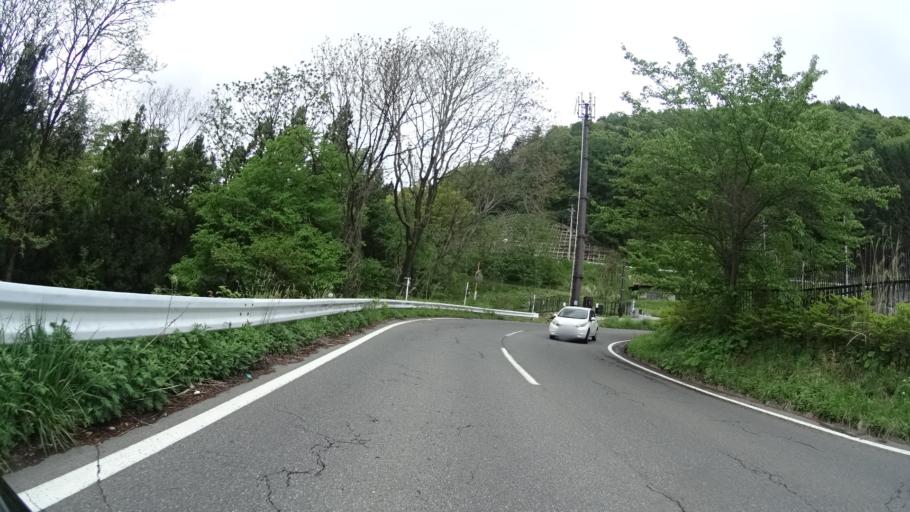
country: JP
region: Nagano
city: Nagano-shi
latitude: 36.6949
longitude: 138.2040
